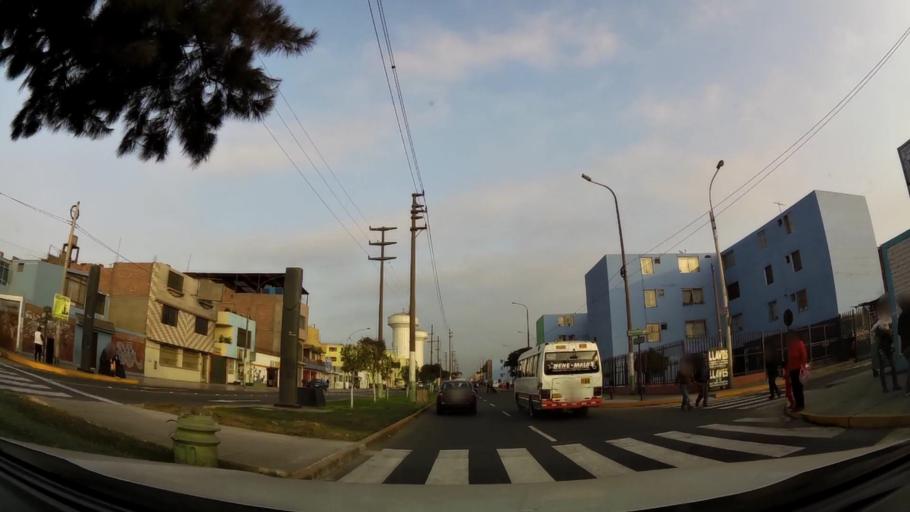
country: PE
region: Callao
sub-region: Callao
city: Callao
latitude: -12.0111
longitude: -77.1013
